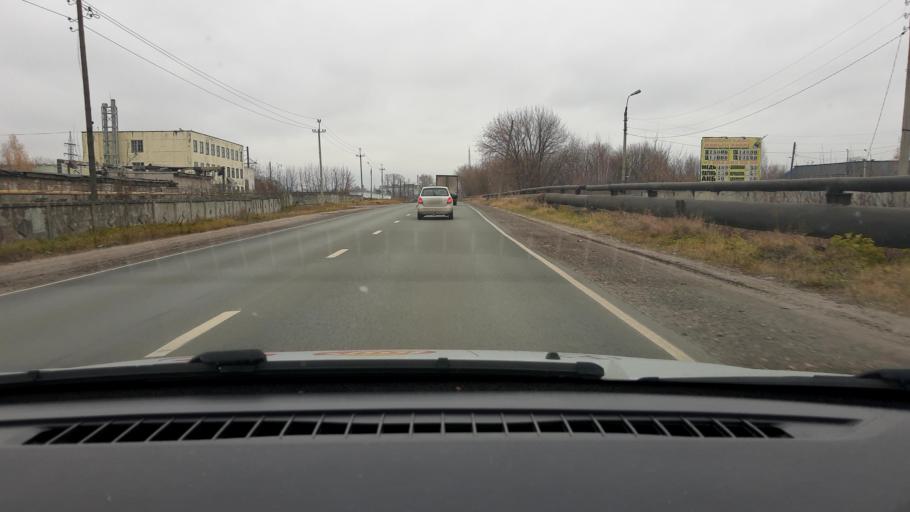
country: RU
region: Nizjnij Novgorod
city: Novaya Balakhna
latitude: 56.4974
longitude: 43.5940
